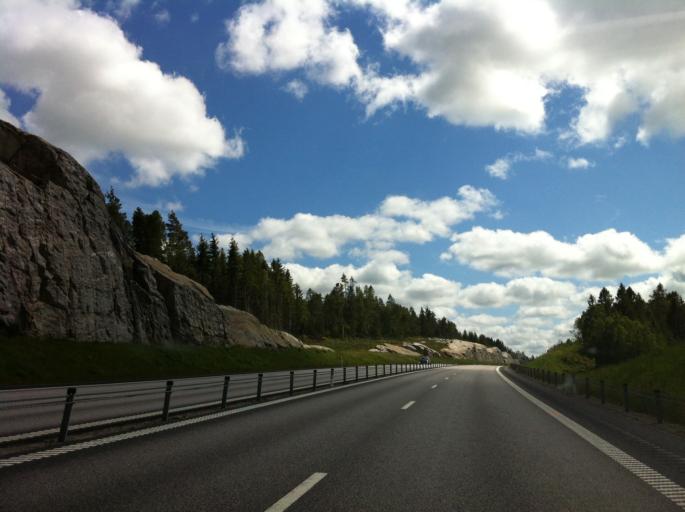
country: SE
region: Vaestra Goetaland
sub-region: Lilla Edets Kommun
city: Lodose
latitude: 58.0602
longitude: 12.1665
